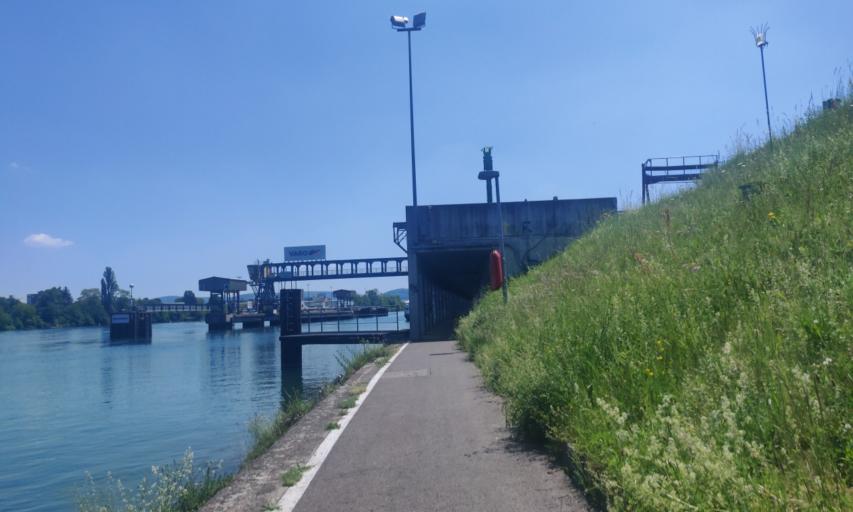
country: CH
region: Basel-Landschaft
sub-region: Bezirk Arlesheim
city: Birsfelden
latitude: 47.5570
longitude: 7.6394
